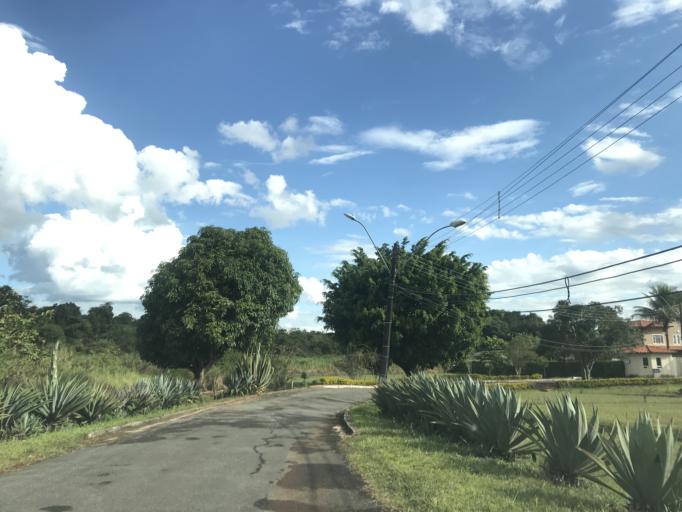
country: BR
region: Federal District
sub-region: Brasilia
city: Brasilia
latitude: -15.9174
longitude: -47.9426
